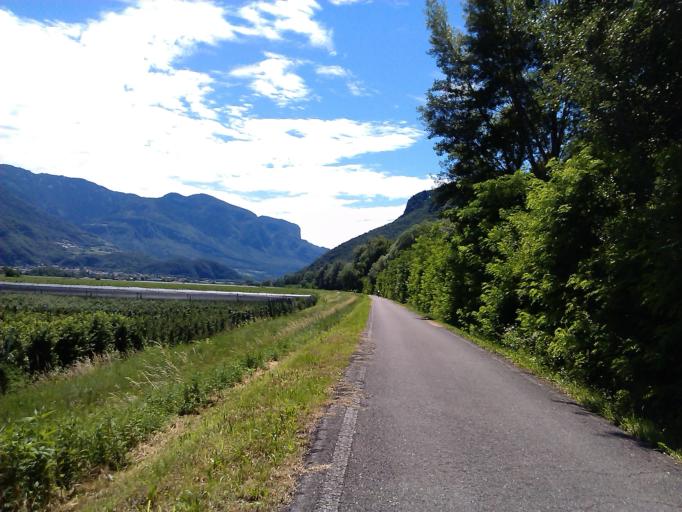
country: IT
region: Trentino-Alto Adige
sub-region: Bolzano
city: Vadena
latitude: 46.3855
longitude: 11.2968
